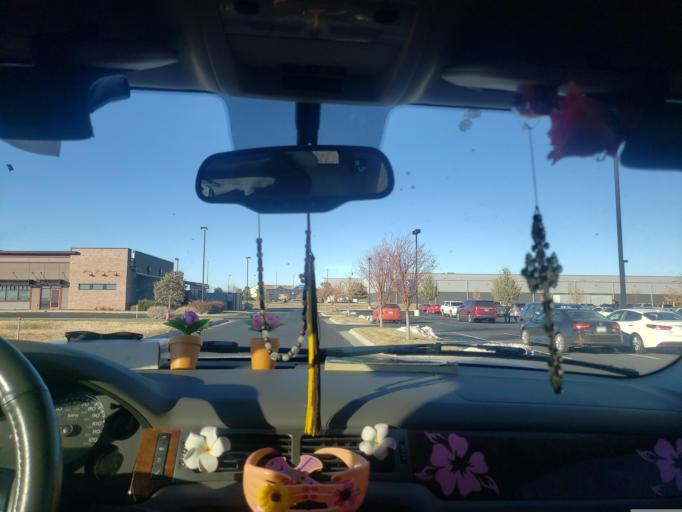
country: US
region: Kansas
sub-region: Finney County
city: Garden City
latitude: 37.9816
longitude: -100.8356
